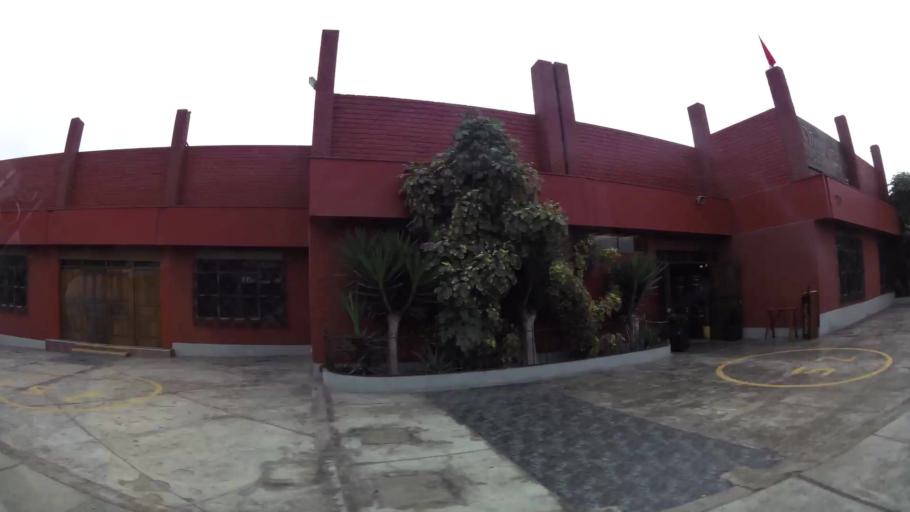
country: PE
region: Lima
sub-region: Lima
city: Surco
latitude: -12.1402
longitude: -77.0179
